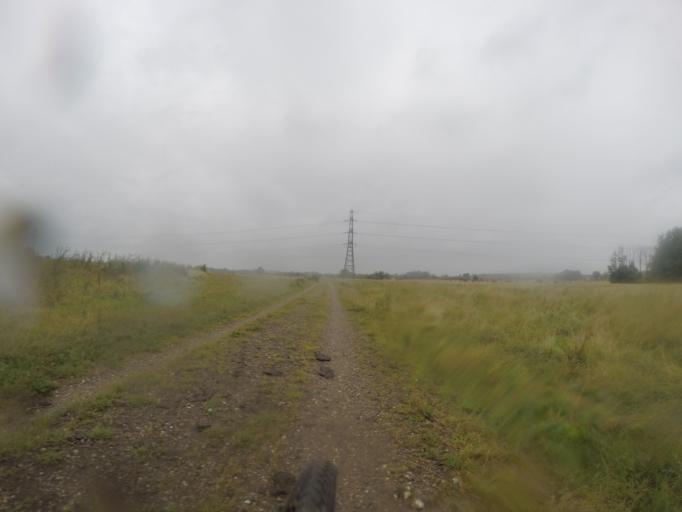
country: DK
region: Capital Region
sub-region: Hoje-Taastrup Kommune
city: Taastrup
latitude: 55.6899
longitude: 12.3120
